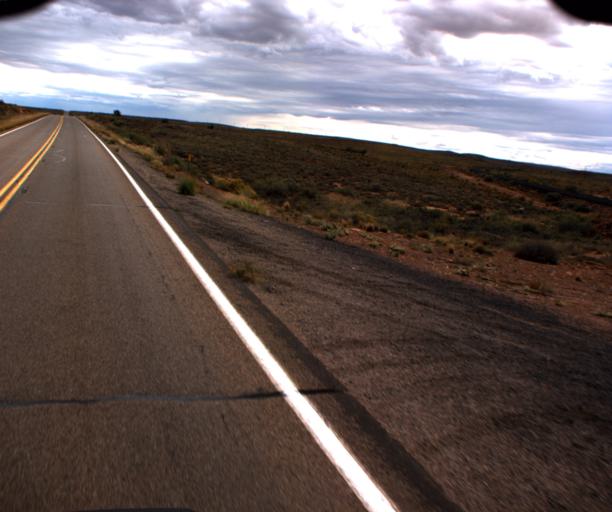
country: US
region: Arizona
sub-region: Navajo County
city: Holbrook
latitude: 34.8447
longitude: -110.1472
